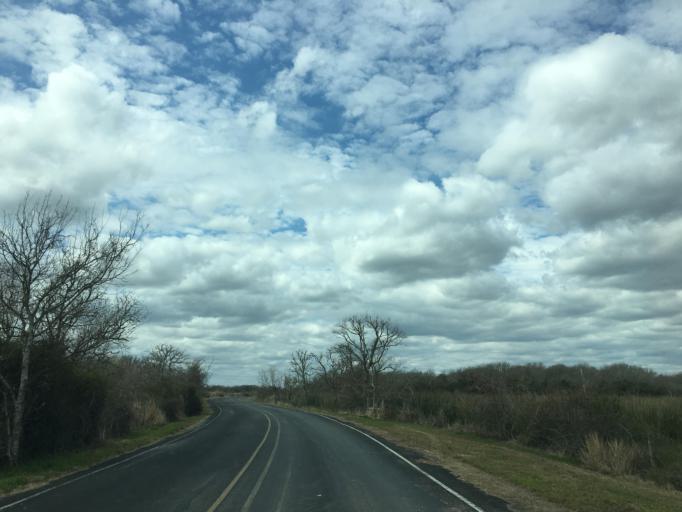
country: US
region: Texas
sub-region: Brazoria County
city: Oyster Creek
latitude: 29.0596
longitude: -95.2722
